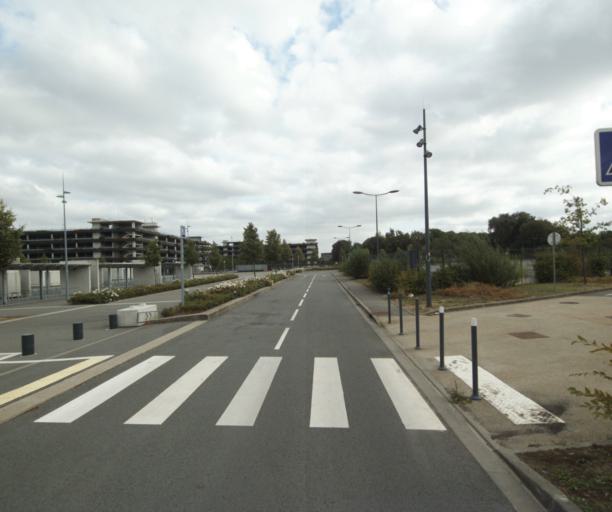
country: FR
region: Nord-Pas-de-Calais
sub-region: Departement du Nord
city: Lezennes
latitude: 50.6109
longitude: 3.1288
